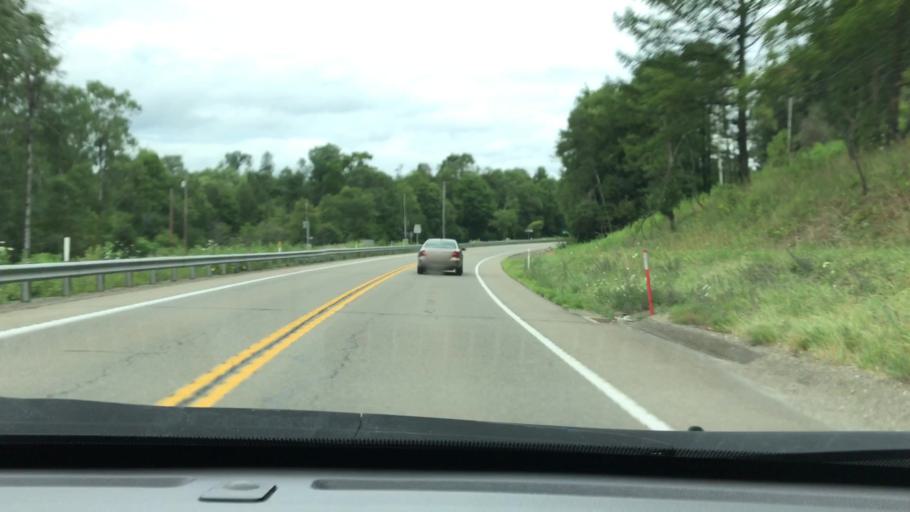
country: US
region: Pennsylvania
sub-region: Elk County
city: Johnsonburg
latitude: 41.5341
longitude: -78.6830
